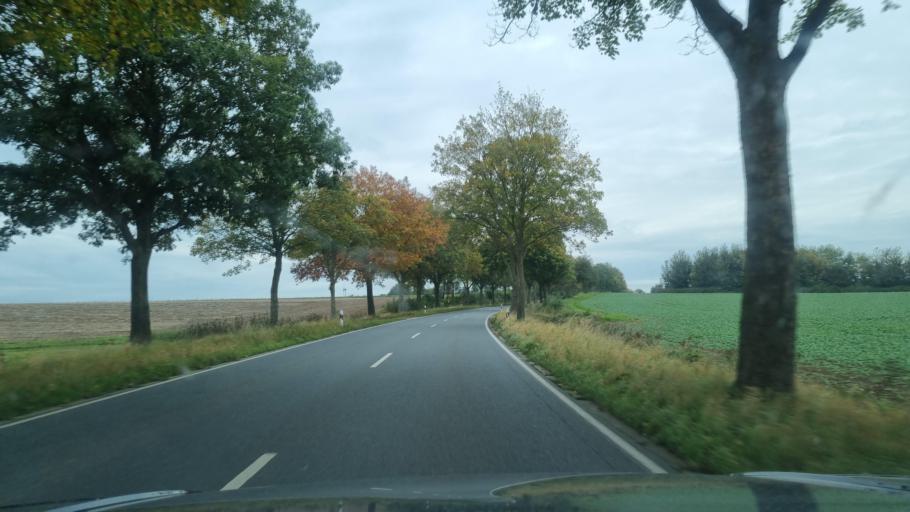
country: DE
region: North Rhine-Westphalia
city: Kalkar
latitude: 51.7092
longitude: 6.3141
